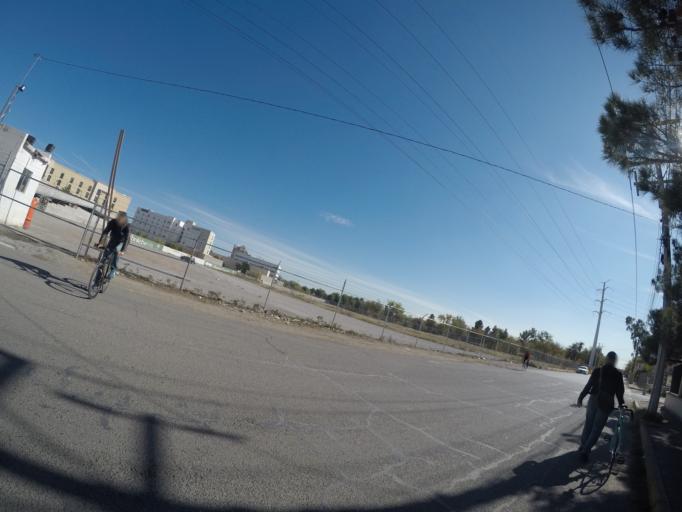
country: MX
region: Chihuahua
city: Ciudad Juarez
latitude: 31.7304
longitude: -106.4128
